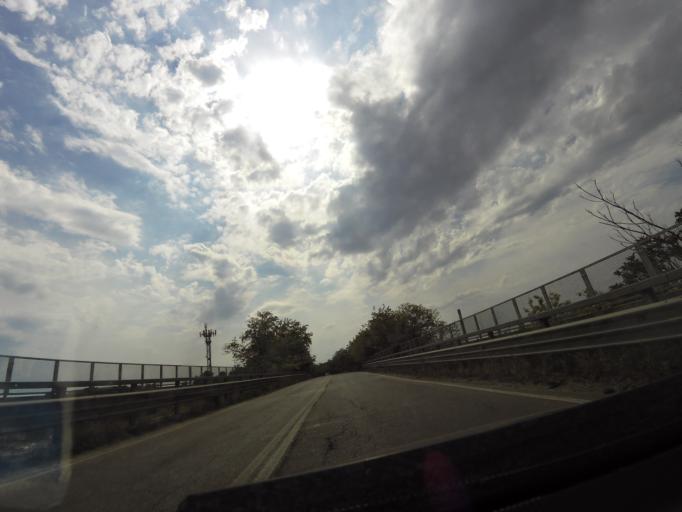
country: IT
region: Lombardy
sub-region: Citta metropolitana di Milano
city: Melegnano
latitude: 45.3626
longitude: 9.3160
